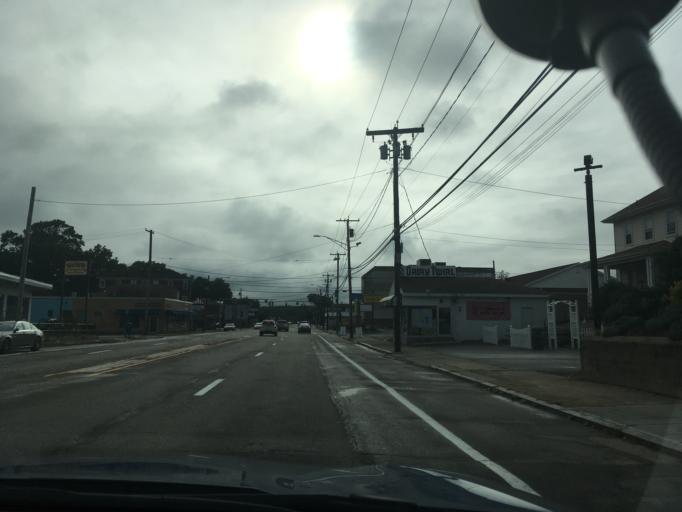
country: US
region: Rhode Island
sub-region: Providence County
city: Cranston
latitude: 41.7791
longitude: -71.4442
